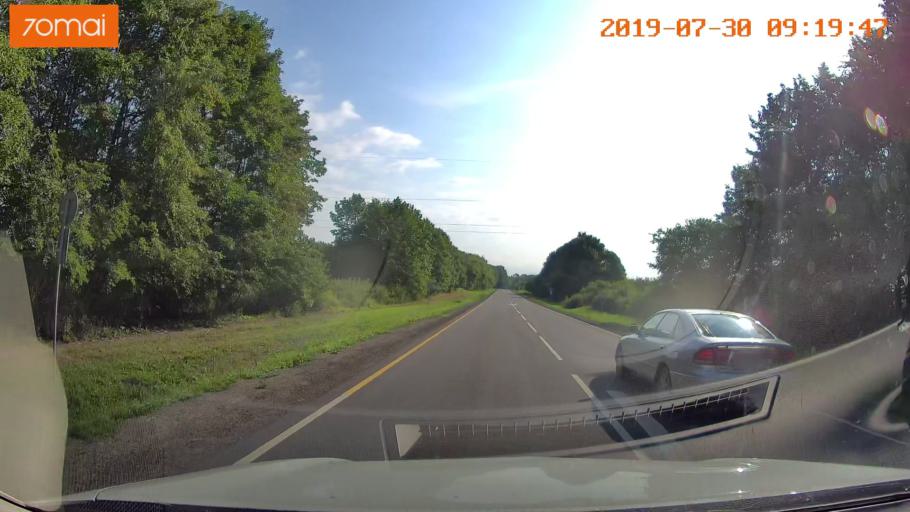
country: RU
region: Kaliningrad
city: Nesterov
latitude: 54.6334
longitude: 22.5975
